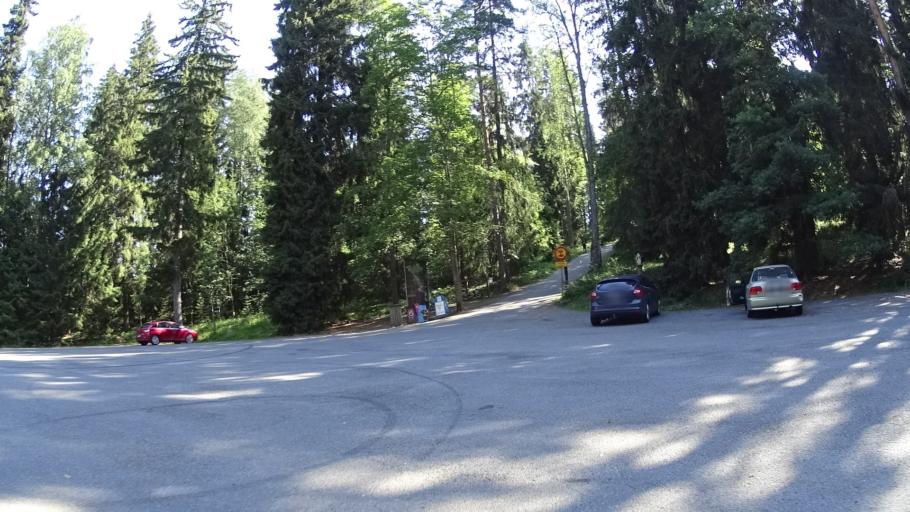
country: FI
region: Haeme
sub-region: Haemeenlinna
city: Haemeenlinna
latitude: 61.0227
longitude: 24.4671
